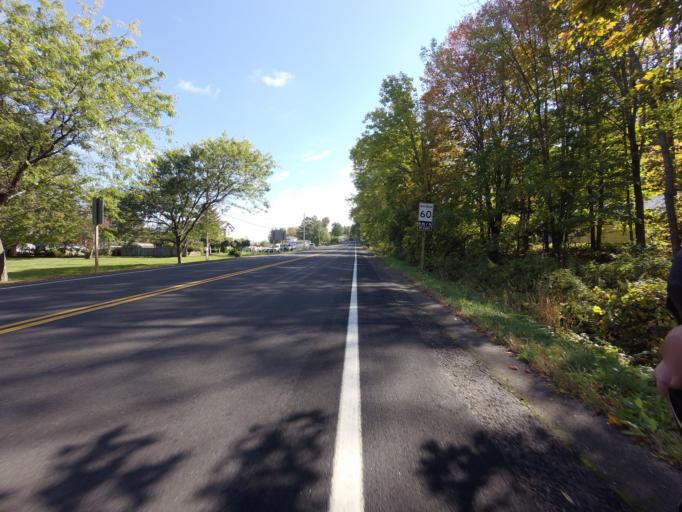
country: CA
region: Ontario
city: Picton
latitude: 44.0438
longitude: -77.0722
